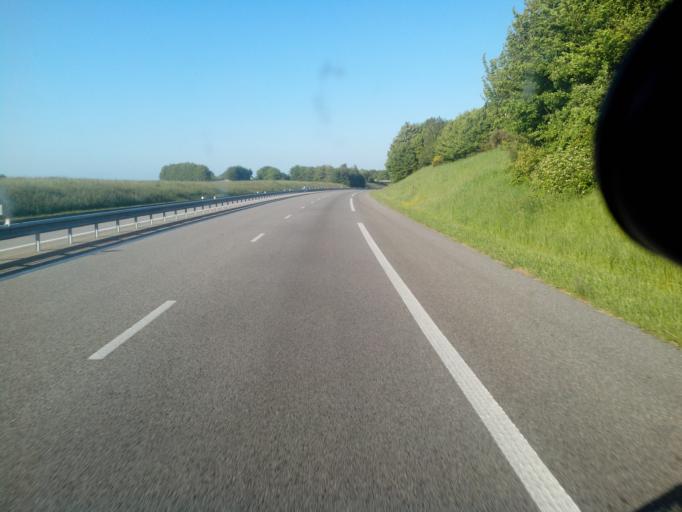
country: FR
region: Haute-Normandie
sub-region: Departement de la Seine-Maritime
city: Beuzeville-la-Grenier
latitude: 49.5771
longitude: 0.4130
